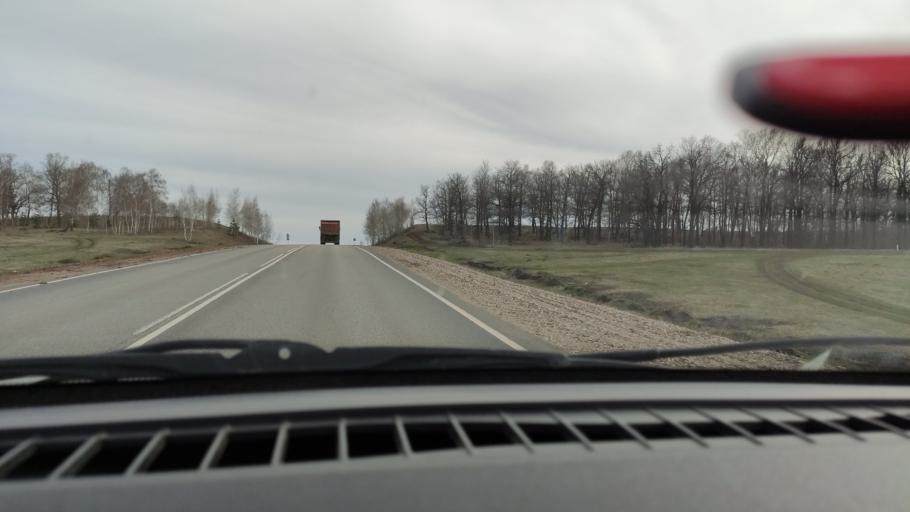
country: RU
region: Bashkortostan
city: Yermolayevo
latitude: 52.7119
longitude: 55.8547
